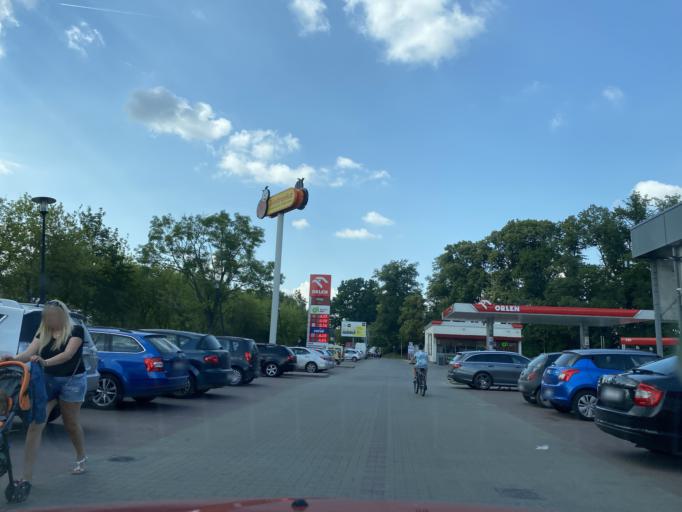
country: PL
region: Greater Poland Voivodeship
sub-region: Powiat poznanski
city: Plewiska
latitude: 52.3815
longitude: 16.7447
